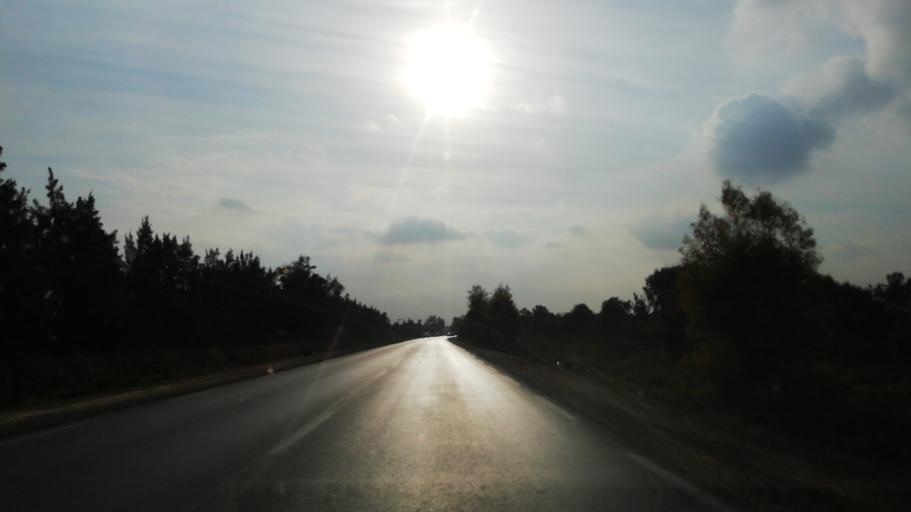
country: DZ
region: Mostaganem
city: Mostaganem
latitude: 35.8421
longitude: 0.0656
